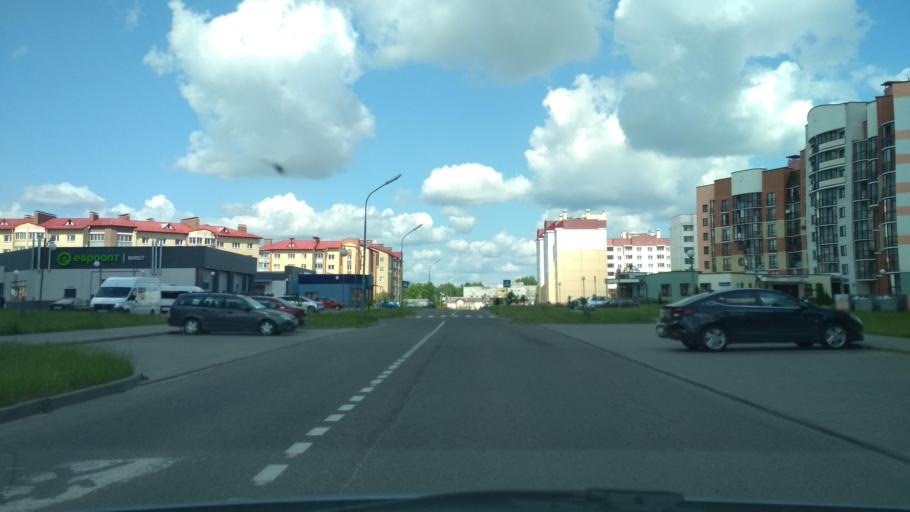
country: BY
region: Grodnenskaya
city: Astravyets
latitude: 54.6069
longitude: 25.9705
